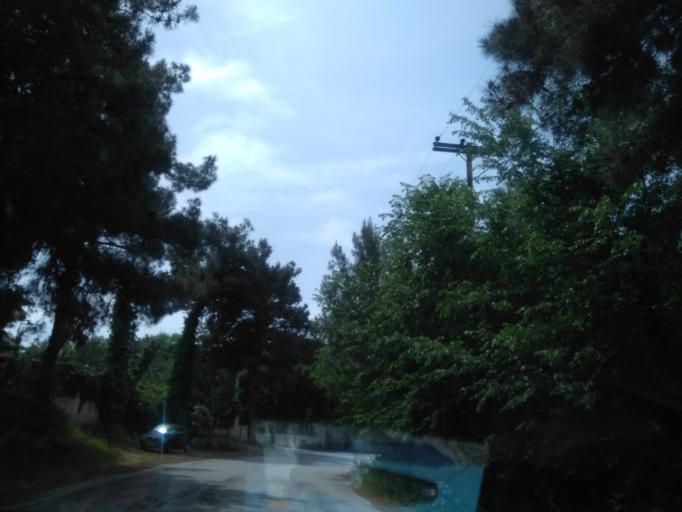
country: GR
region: Central Macedonia
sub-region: Nomos Thessalonikis
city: Lagyna
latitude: 40.7248
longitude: 22.9955
